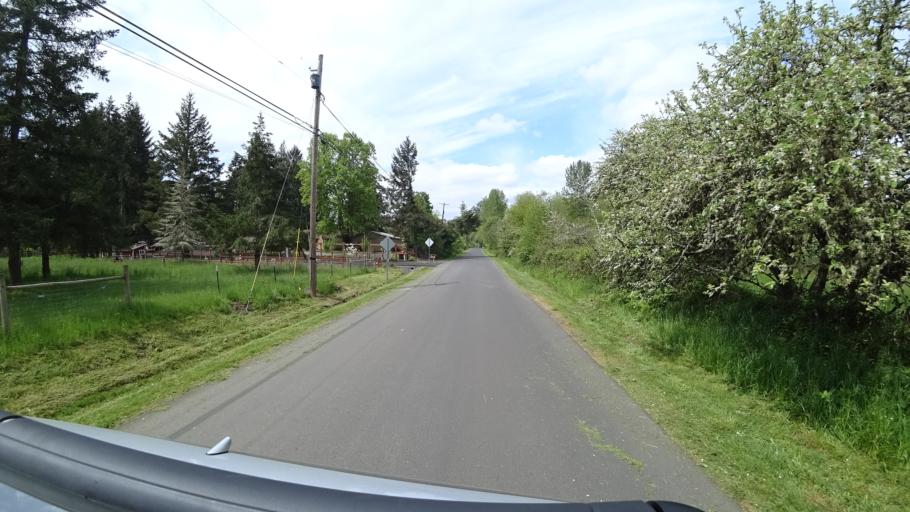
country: US
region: Oregon
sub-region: Washington County
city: Hillsboro
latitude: 45.5326
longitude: -123.0014
